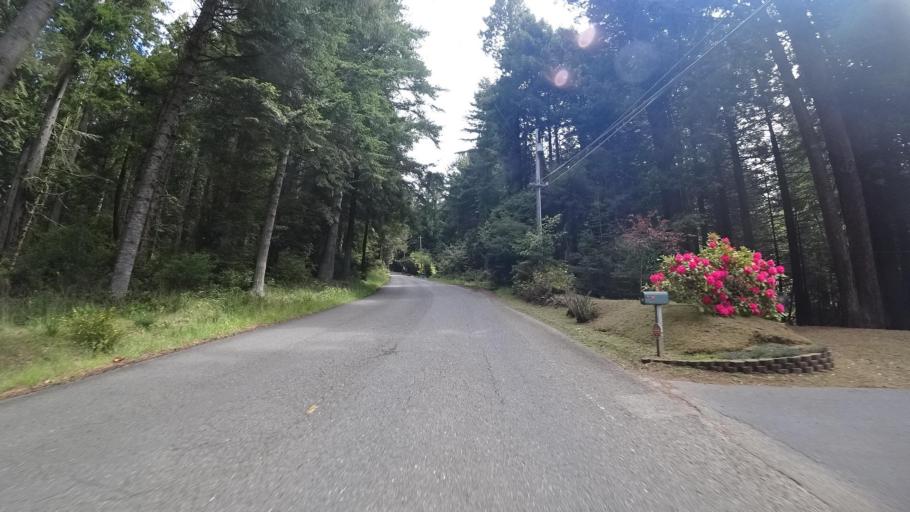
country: US
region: California
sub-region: Humboldt County
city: Arcata
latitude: 40.8691
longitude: -124.0645
